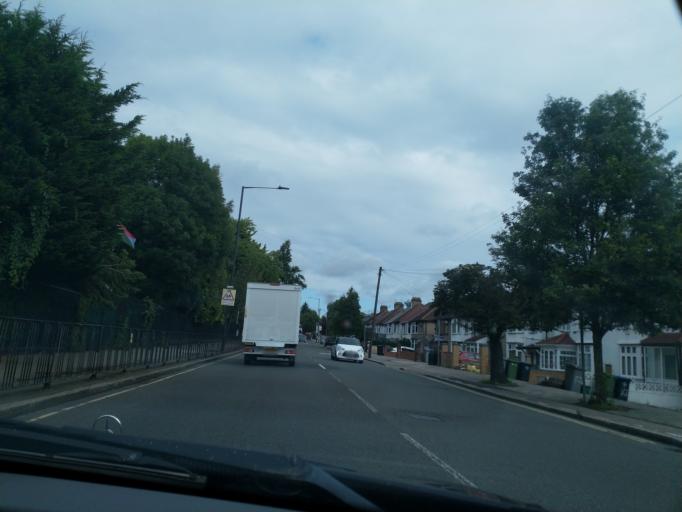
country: GB
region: England
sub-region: Greater London
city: Harrow on the Hill
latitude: 51.5589
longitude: -0.3186
